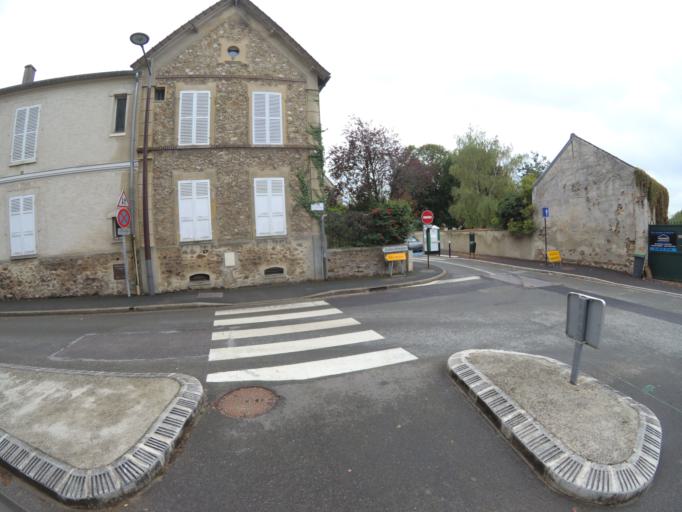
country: FR
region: Ile-de-France
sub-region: Departement de Seine-et-Marne
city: Bussy-Saint-Georges
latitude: 48.8423
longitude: 2.6978
